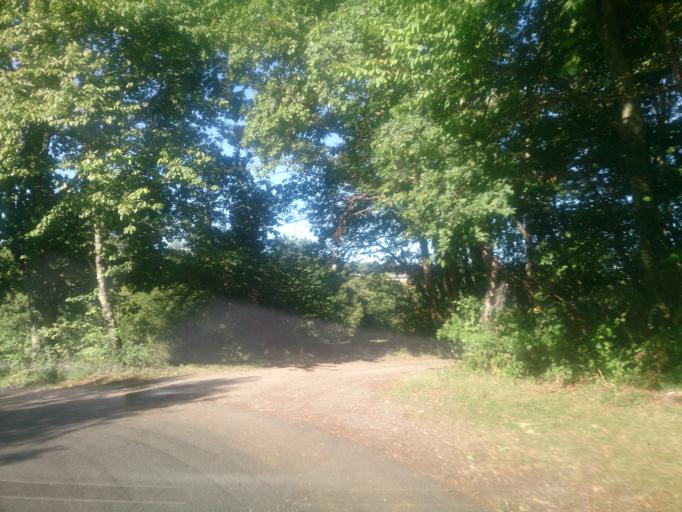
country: FR
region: Midi-Pyrenees
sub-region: Departement des Hautes-Pyrenees
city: Odos
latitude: 43.1431
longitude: 0.0507
